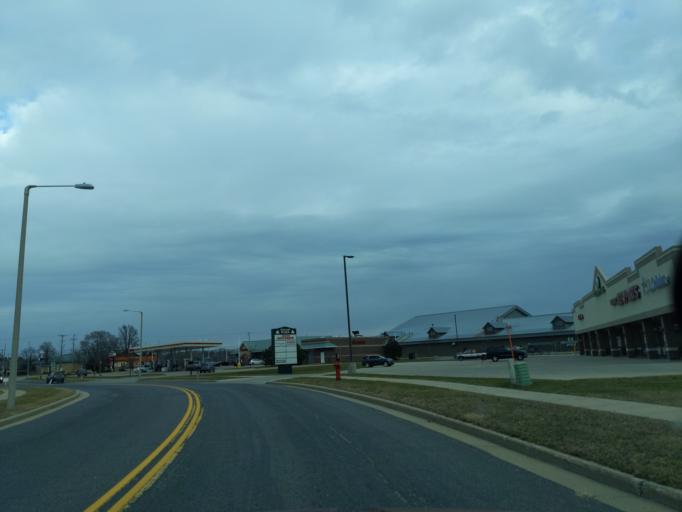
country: US
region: Wisconsin
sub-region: Waushara County
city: Wautoma
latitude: 44.0690
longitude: -89.2726
